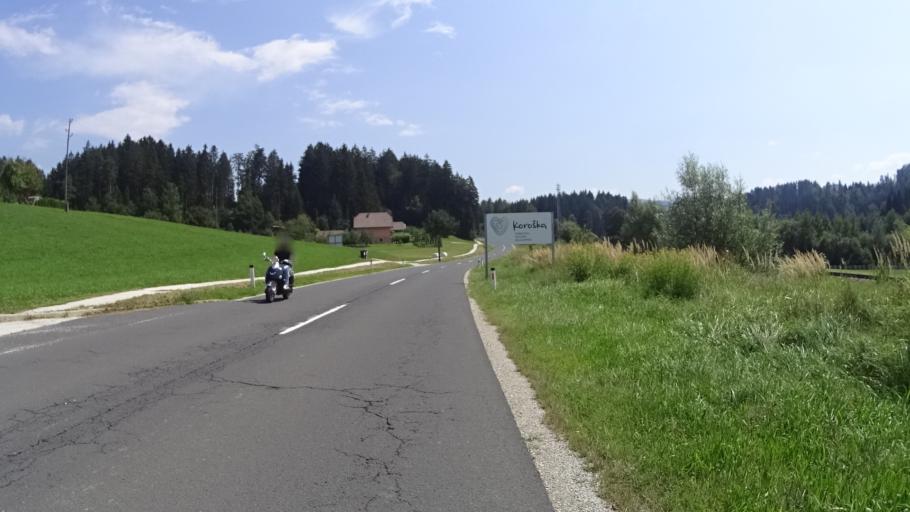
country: SI
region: Mezica
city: Mezica
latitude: 46.5658
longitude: 14.8430
